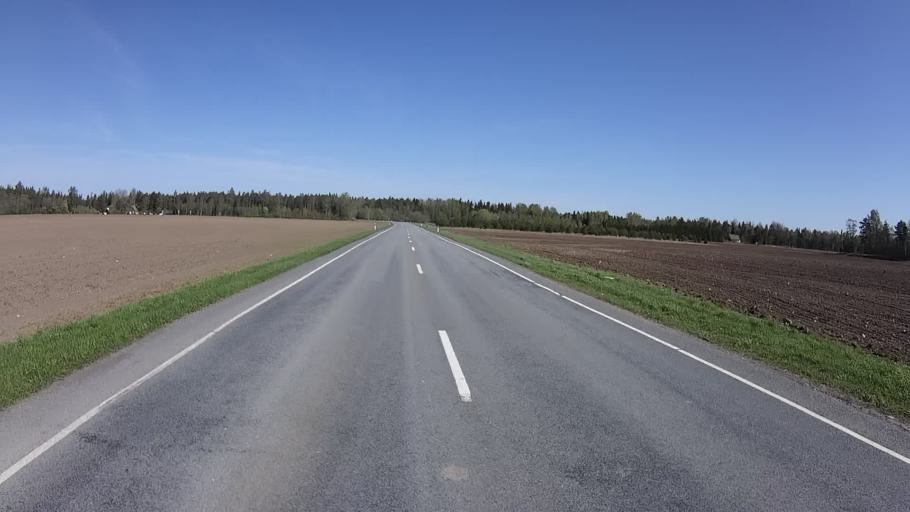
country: EE
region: Raplamaa
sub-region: Jaervakandi vald
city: Jarvakandi
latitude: 58.8456
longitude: 24.7961
